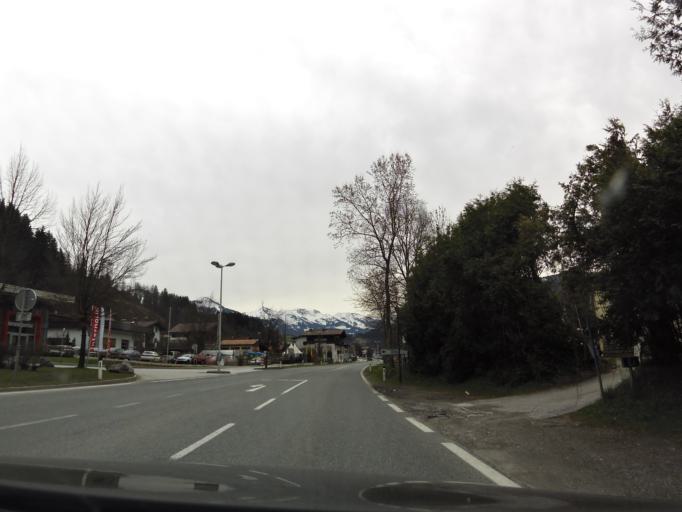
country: AT
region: Tyrol
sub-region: Politischer Bezirk Kitzbuhel
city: Itter
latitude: 47.4572
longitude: 12.1484
